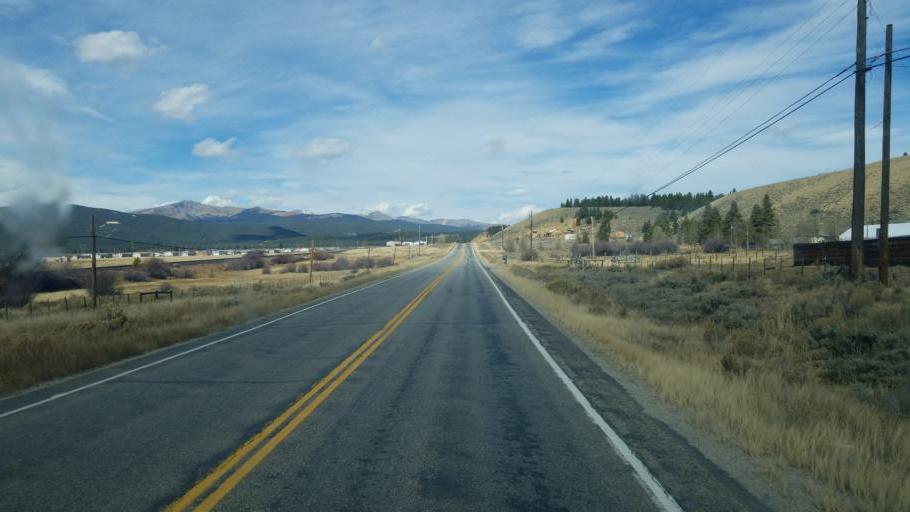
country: US
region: Colorado
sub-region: Lake County
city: Leadville North
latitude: 39.2132
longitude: -106.3466
